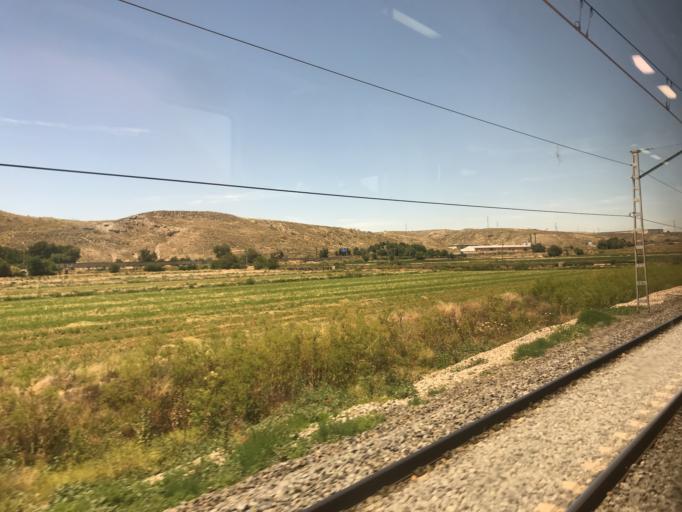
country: ES
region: Madrid
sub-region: Provincia de Madrid
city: Aranjuez
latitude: 40.0792
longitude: -3.6342
